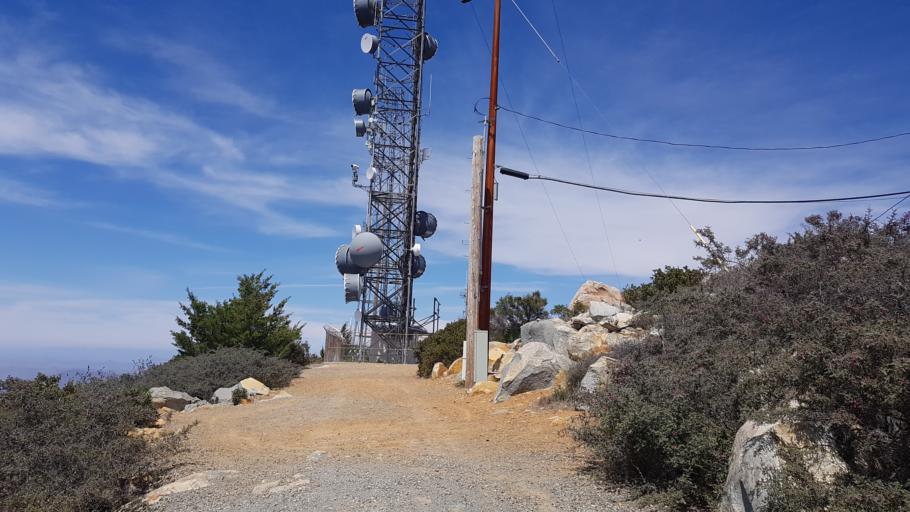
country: MX
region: Baja California
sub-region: Tijuana
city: El Nino
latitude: 32.5944
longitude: -116.8448
